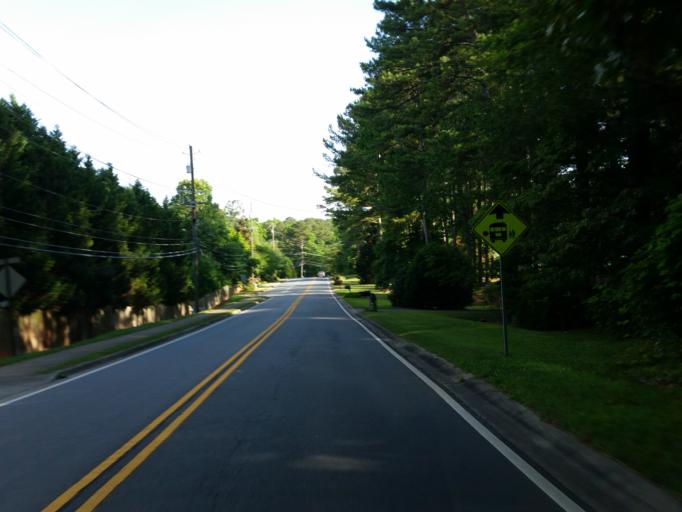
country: US
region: Georgia
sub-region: Cherokee County
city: Woodstock
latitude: 34.0676
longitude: -84.4848
